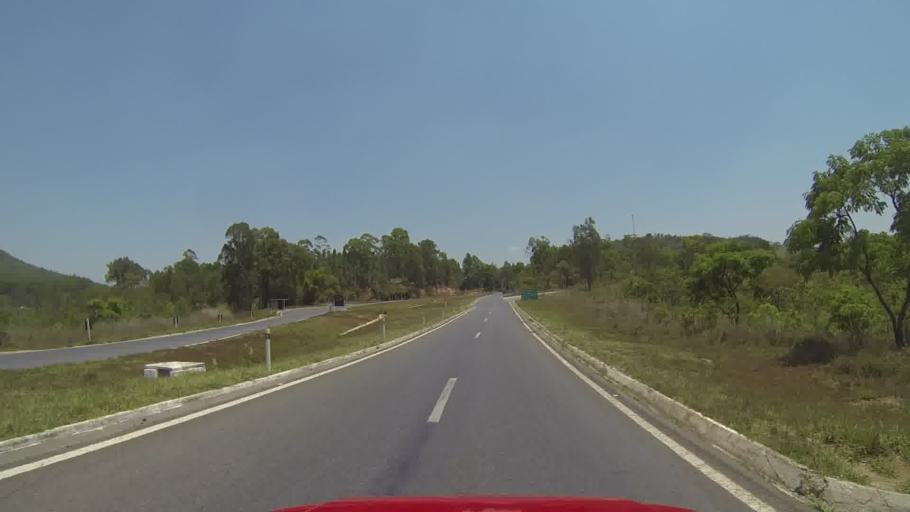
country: BR
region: Minas Gerais
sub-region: Itapecerica
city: Itapecerica
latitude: -20.2969
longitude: -45.1803
